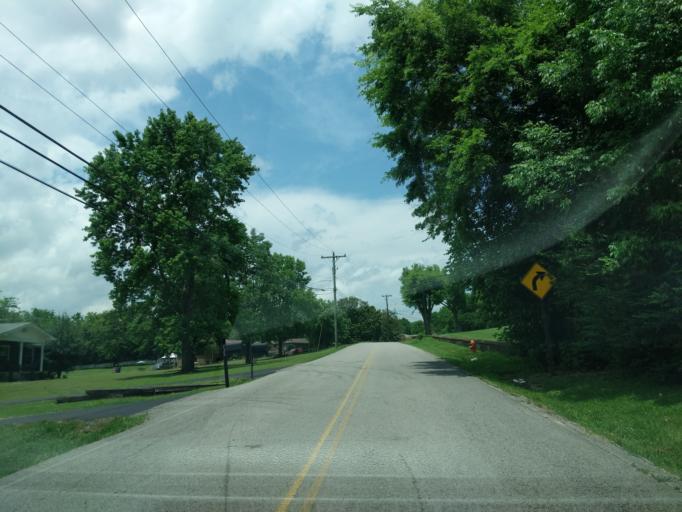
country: US
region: Tennessee
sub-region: Davidson County
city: Goodlettsville
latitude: 36.3015
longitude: -86.7300
